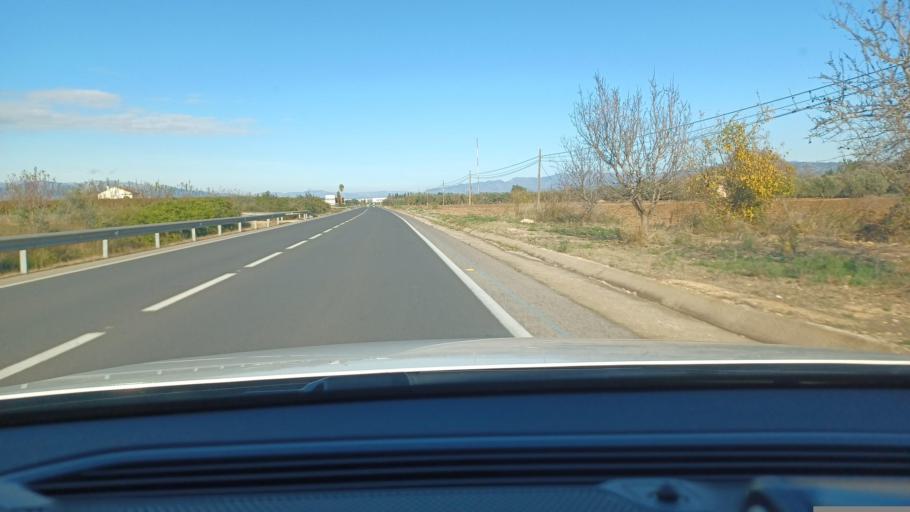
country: ES
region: Catalonia
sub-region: Provincia de Tarragona
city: Santa Barbara
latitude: 40.7273
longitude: 0.5033
